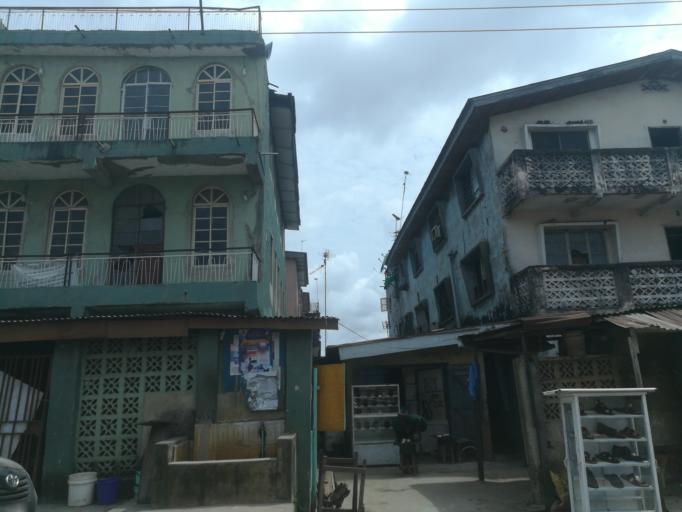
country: NG
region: Lagos
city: Somolu
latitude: 6.5247
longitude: 3.3833
